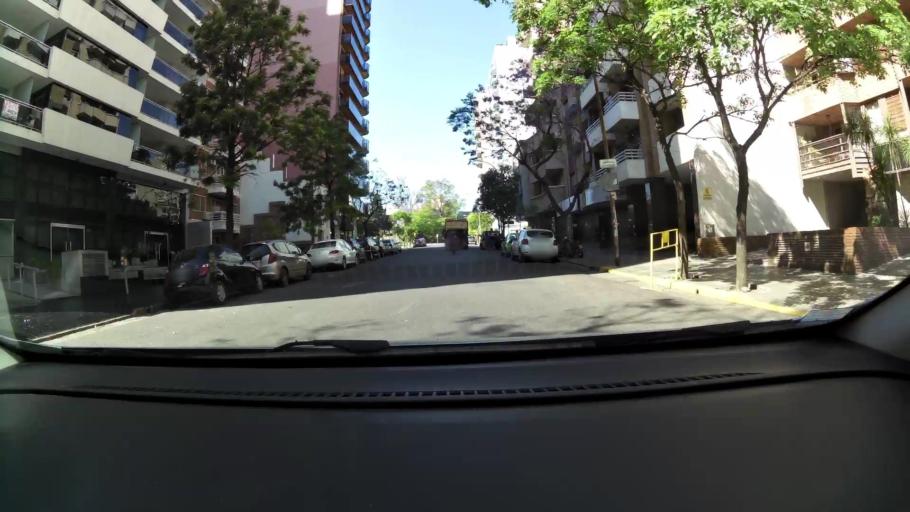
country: AR
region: Cordoba
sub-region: Departamento de Capital
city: Cordoba
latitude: -31.4266
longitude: -64.1825
